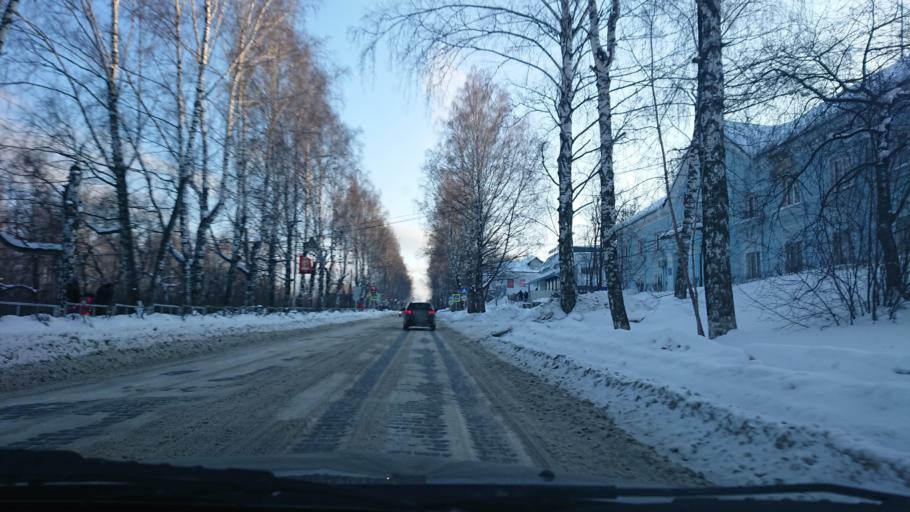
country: RU
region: Sverdlovsk
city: Degtyarsk
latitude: 56.6962
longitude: 60.0882
